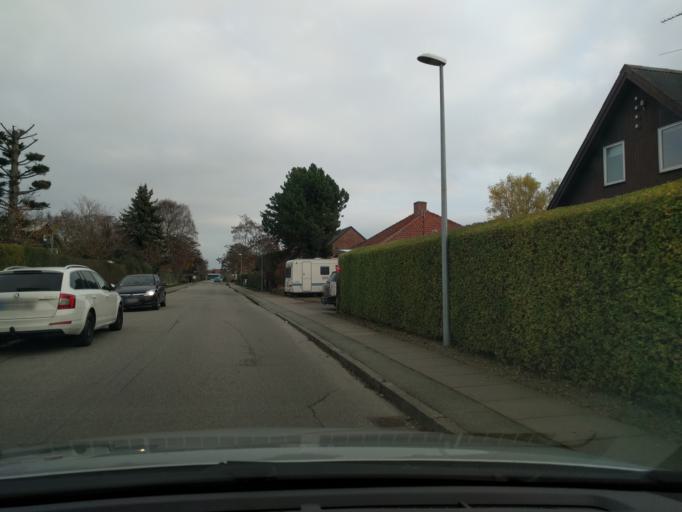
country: DK
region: Capital Region
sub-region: Tarnby Kommune
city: Tarnby
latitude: 55.6344
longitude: 12.5942
